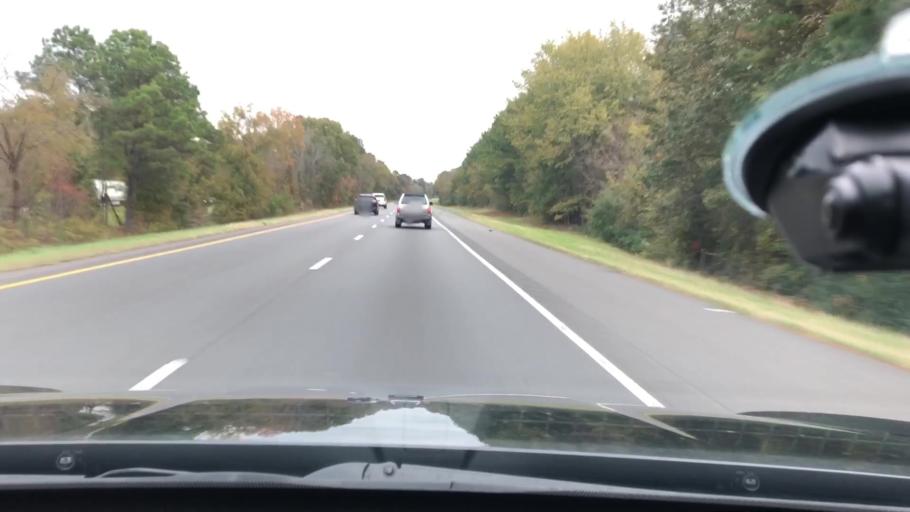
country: US
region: Arkansas
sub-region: Hempstead County
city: Hope
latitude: 33.7115
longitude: -93.5699
